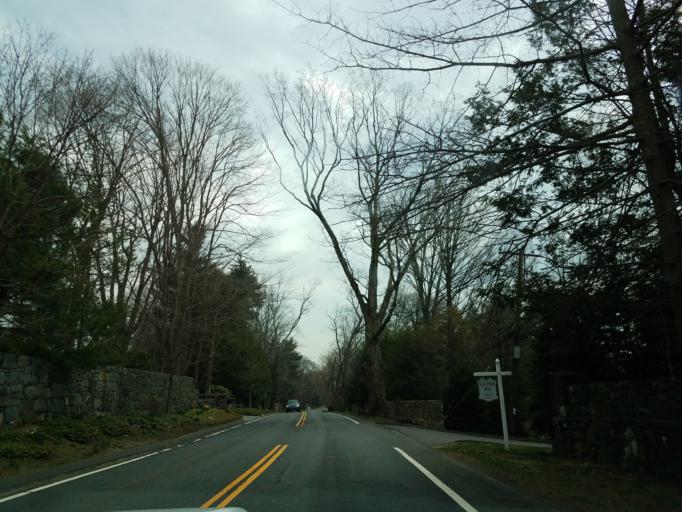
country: US
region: Connecticut
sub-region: Fairfield County
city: Greenwich
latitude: 41.0424
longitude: -73.6354
